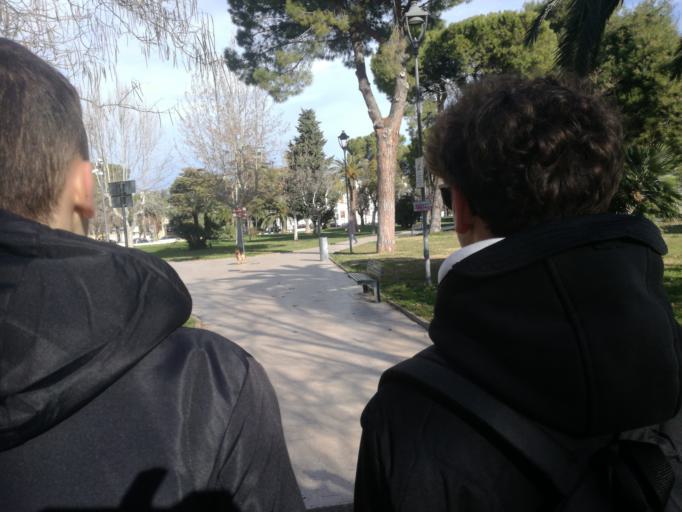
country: IT
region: Apulia
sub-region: Provincia di Barletta - Andria - Trani
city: Andria
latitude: 41.2329
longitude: 16.3080
